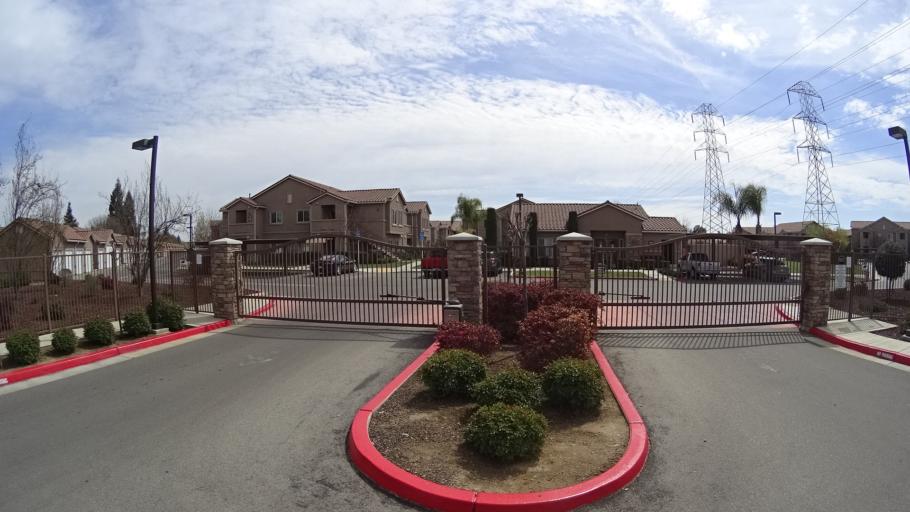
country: US
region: California
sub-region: Fresno County
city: West Park
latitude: 36.8188
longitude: -119.8763
